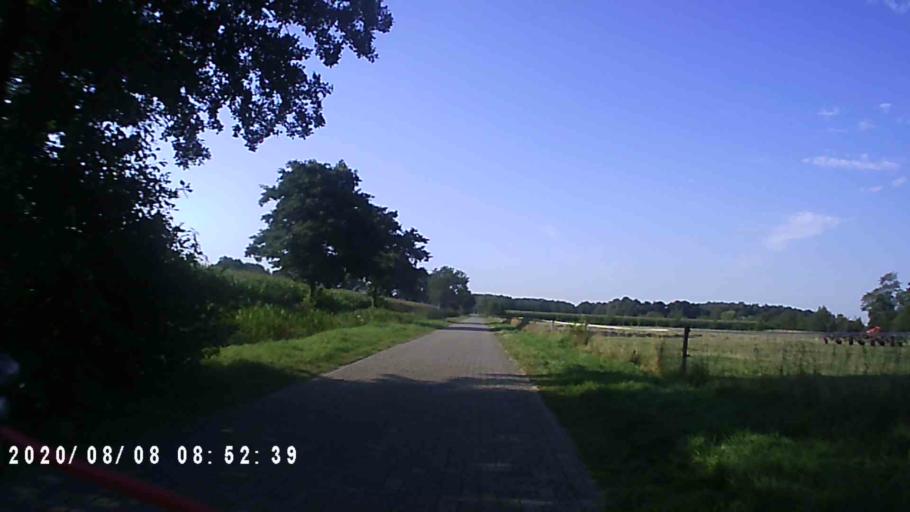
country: NL
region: Groningen
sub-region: Gemeente Leek
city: Leek
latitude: 53.0643
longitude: 6.3261
